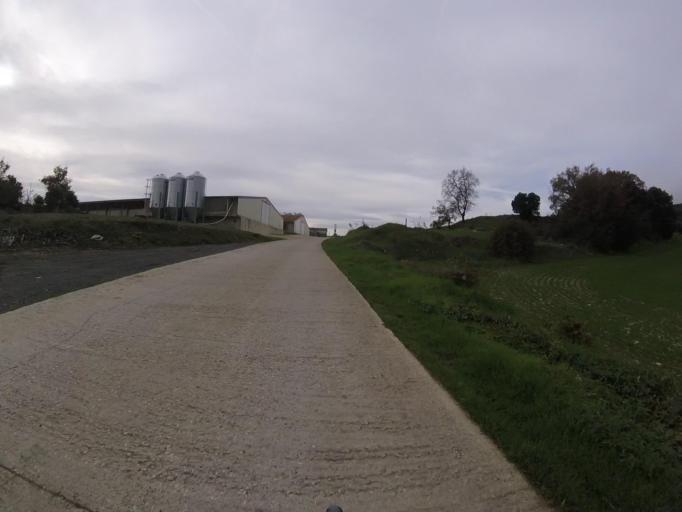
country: ES
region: Navarre
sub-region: Provincia de Navarra
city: Estella
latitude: 42.7217
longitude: -2.0295
